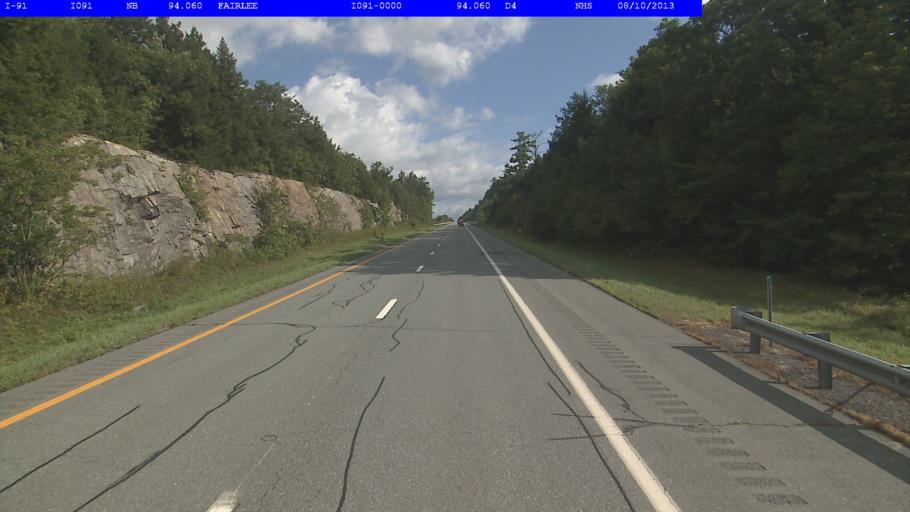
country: US
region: New Hampshire
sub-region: Grafton County
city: Orford
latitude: 43.9339
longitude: -72.1337
